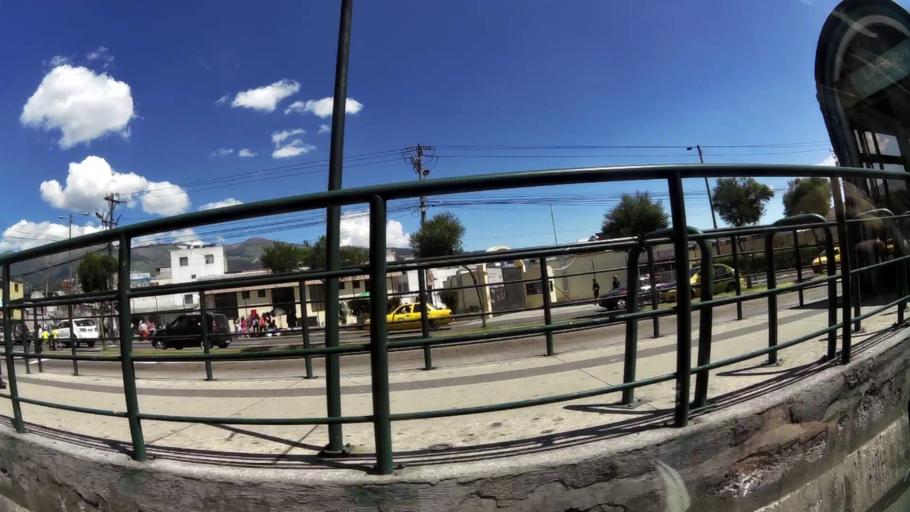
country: EC
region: Pichincha
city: Quito
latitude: -0.1150
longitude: -78.4906
